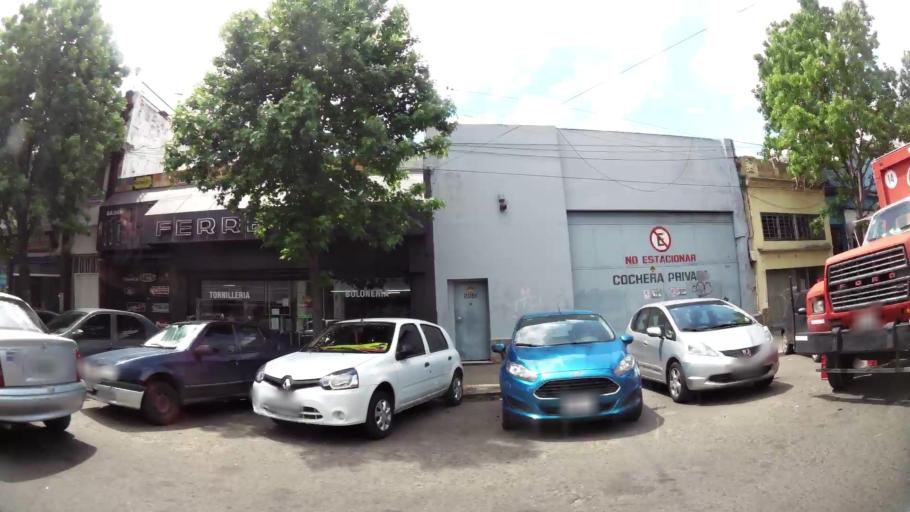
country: AR
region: Santa Fe
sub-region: Departamento de Rosario
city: Rosario
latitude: -32.9617
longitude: -60.6404
